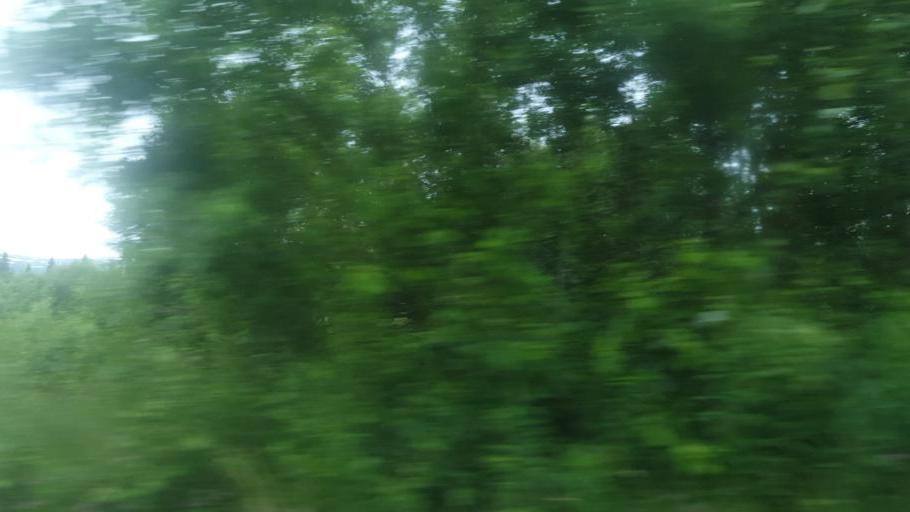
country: NO
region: Oppland
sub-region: Vestre Slidre
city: Slidre
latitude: 61.2410
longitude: 8.9178
